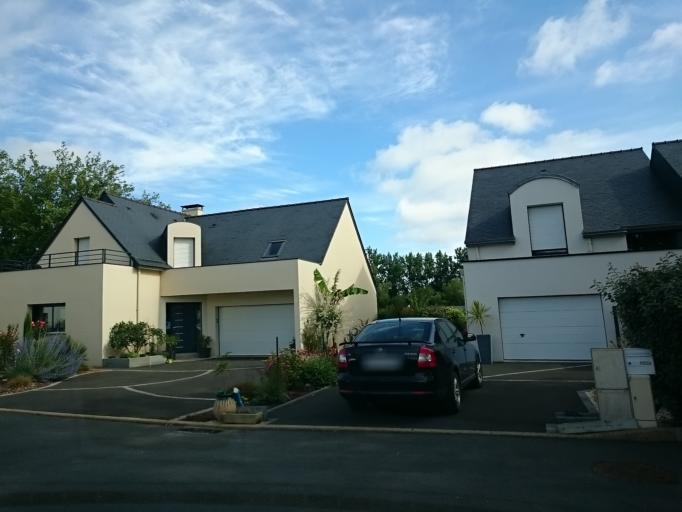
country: FR
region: Brittany
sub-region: Departement d'Ille-et-Vilaine
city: Crevin
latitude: 47.9426
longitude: -1.6502
